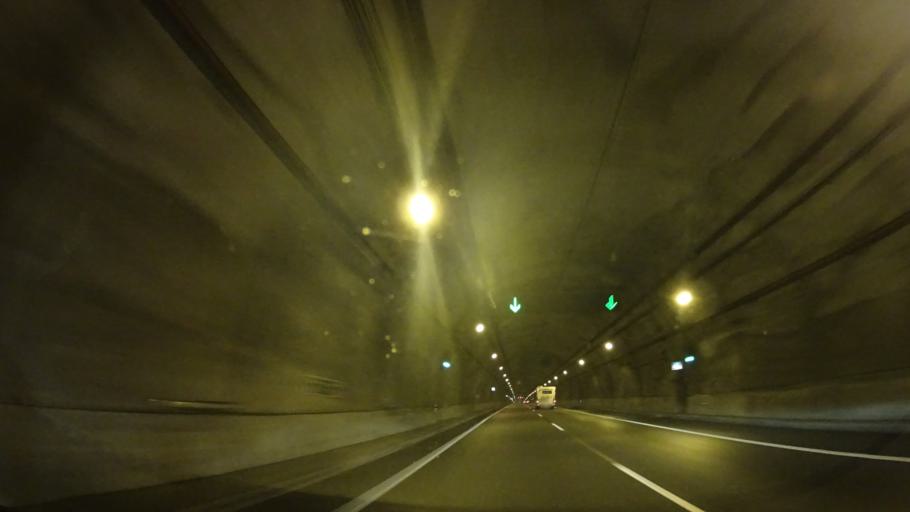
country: ES
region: Asturias
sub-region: Province of Asturias
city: Arriba
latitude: 43.4659
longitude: -5.5199
